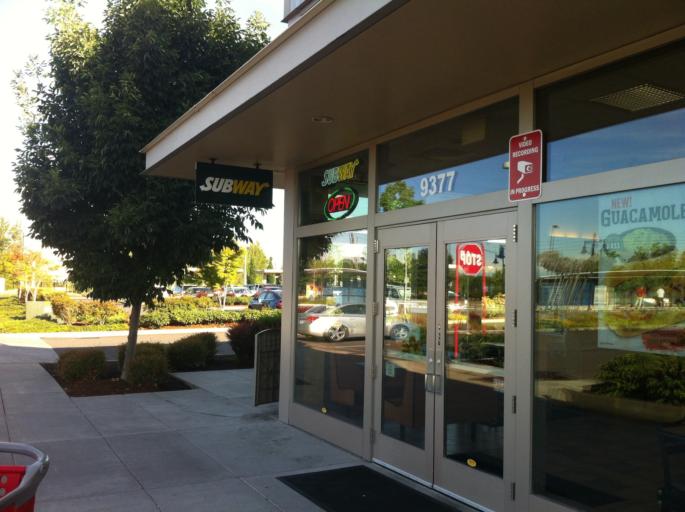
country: US
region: Washington
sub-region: Clark County
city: Orchards
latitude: 45.5772
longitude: -122.5663
